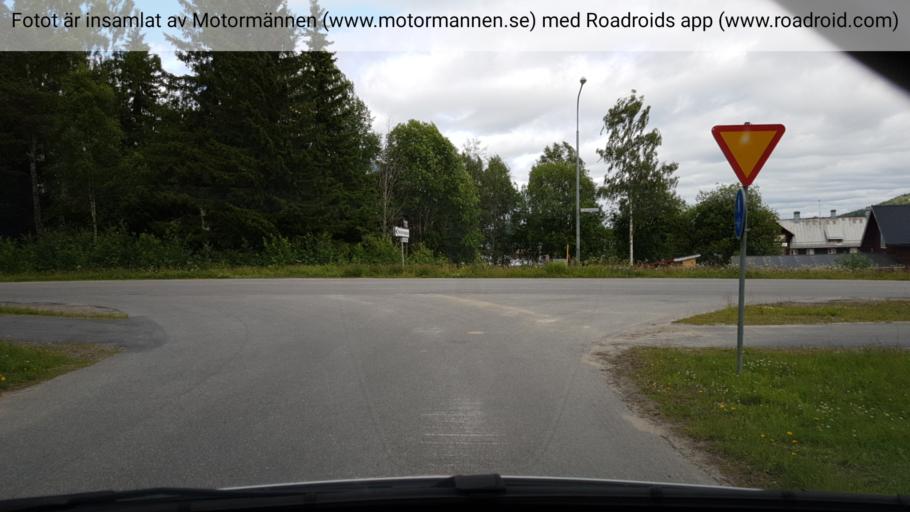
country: SE
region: Vaesterbotten
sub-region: Vannas Kommun
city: Vaennaes
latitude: 63.9084
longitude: 19.7467
